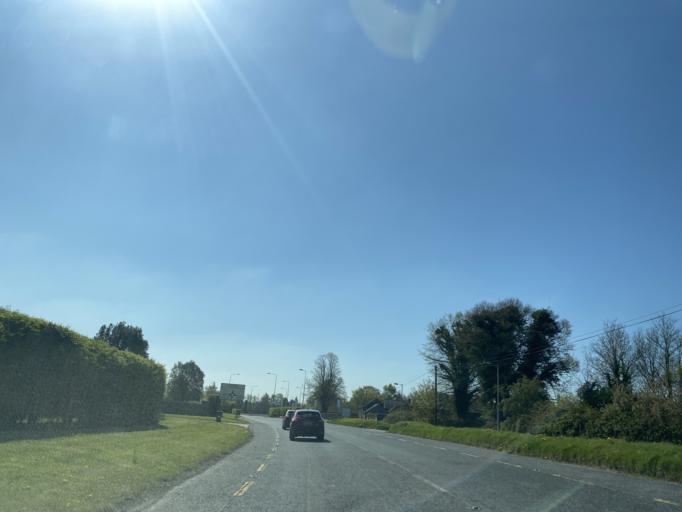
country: IE
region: Leinster
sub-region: Kildare
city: Maynooth
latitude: 53.3253
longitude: -6.6079
